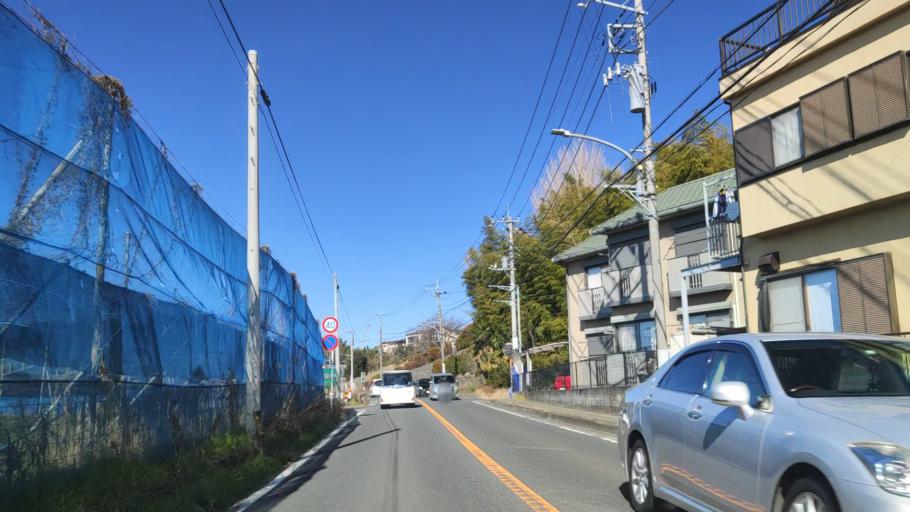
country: JP
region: Tokyo
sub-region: Machida-shi
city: Machida
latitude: 35.5244
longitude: 139.5335
